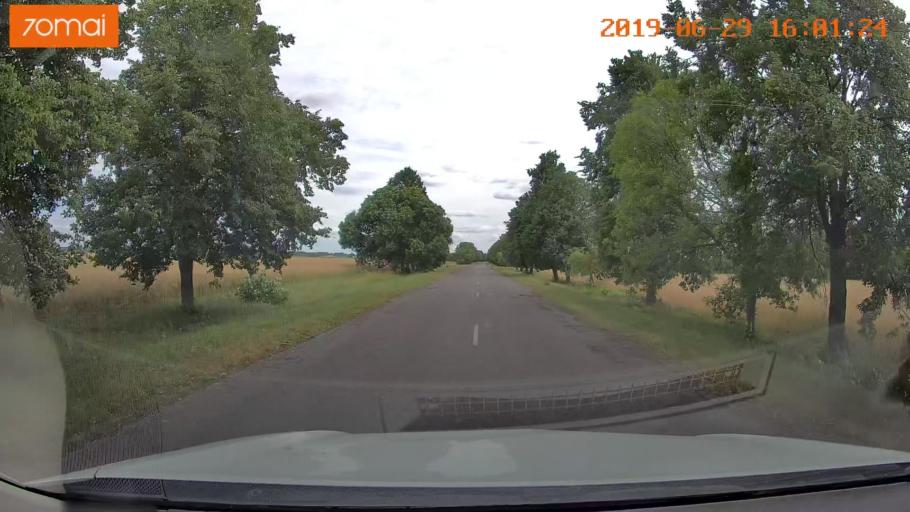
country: BY
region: Brest
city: Luninyets
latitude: 52.2478
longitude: 27.0166
